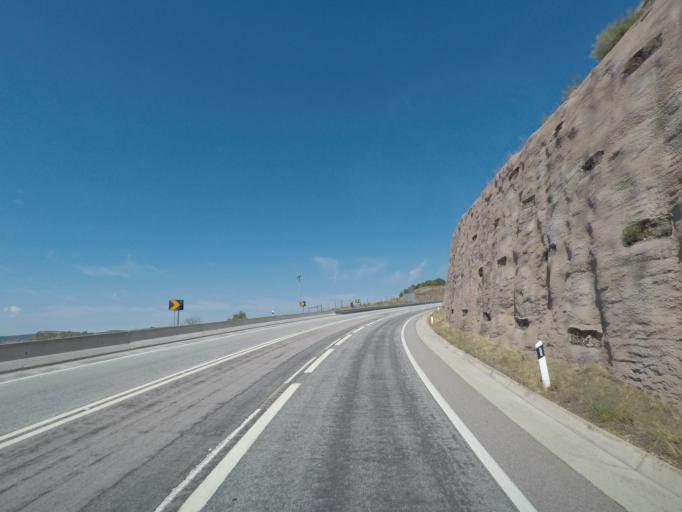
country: PT
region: Braganca
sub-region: Alfandega da Fe
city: Alfandega da Fe
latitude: 41.2767
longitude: -6.8935
